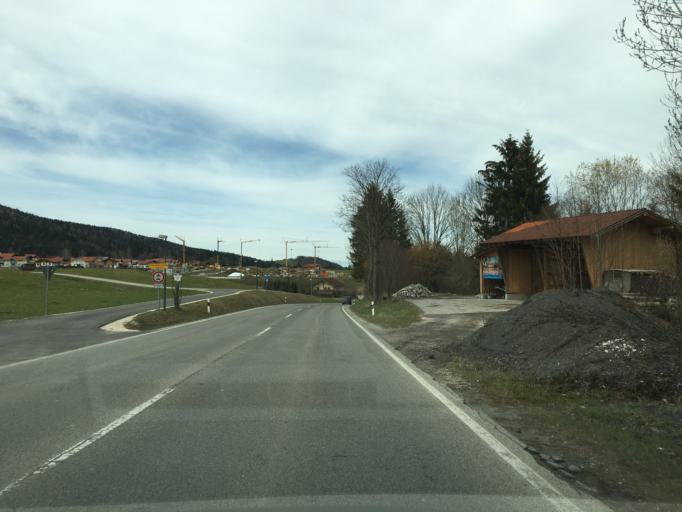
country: DE
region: Bavaria
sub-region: Upper Bavaria
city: Inzell
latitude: 47.7821
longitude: 12.7345
